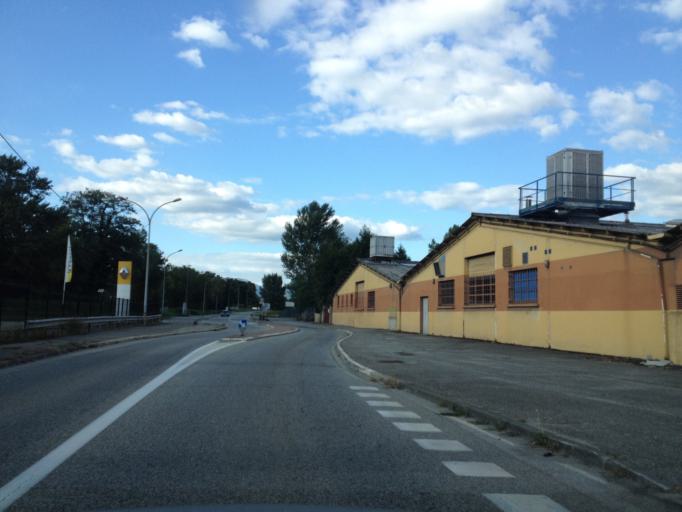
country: FR
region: Rhone-Alpes
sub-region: Departement de l'Isere
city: Pontcharra
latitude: 45.4318
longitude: 6.0050
